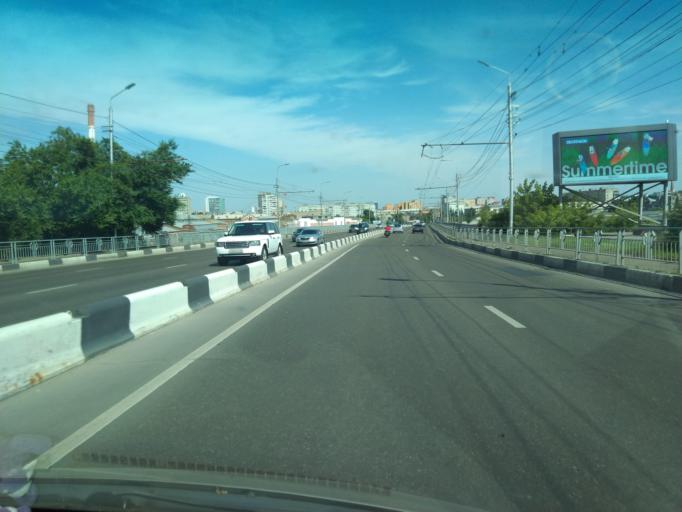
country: RU
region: Krasnoyarskiy
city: Krasnoyarsk
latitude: 56.0125
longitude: 92.8289
